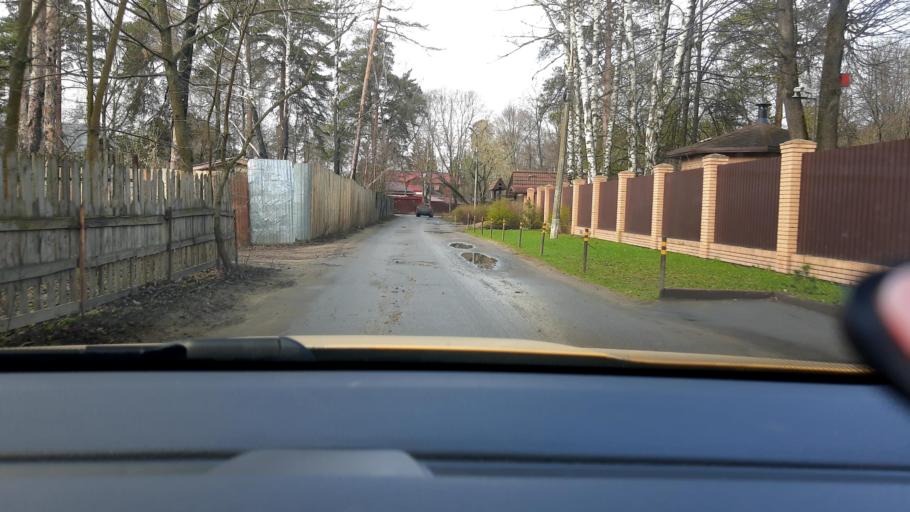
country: RU
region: Moskovskaya
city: Druzhba
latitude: 55.8953
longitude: 37.7419
